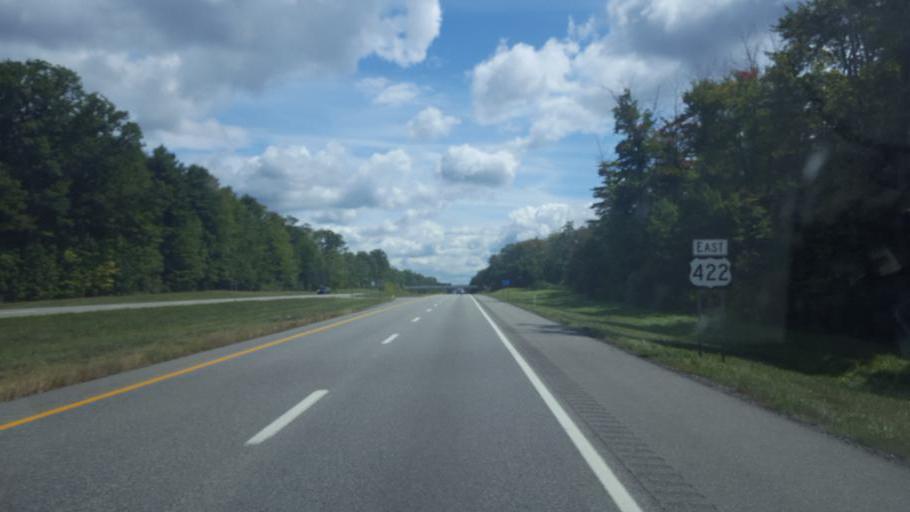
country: US
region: Ohio
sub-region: Geauga County
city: Bainbridge
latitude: 41.3863
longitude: -81.3296
